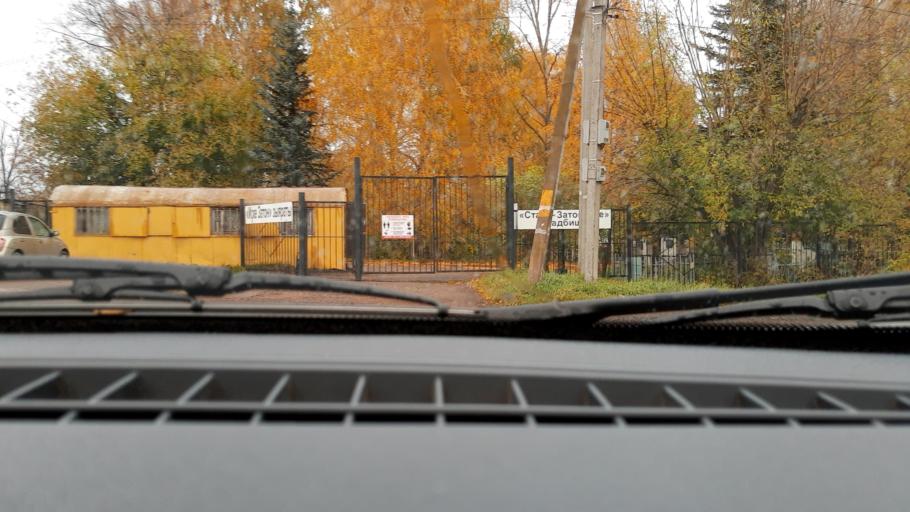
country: RU
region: Bashkortostan
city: Mikhaylovka
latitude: 54.7840
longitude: 55.8931
